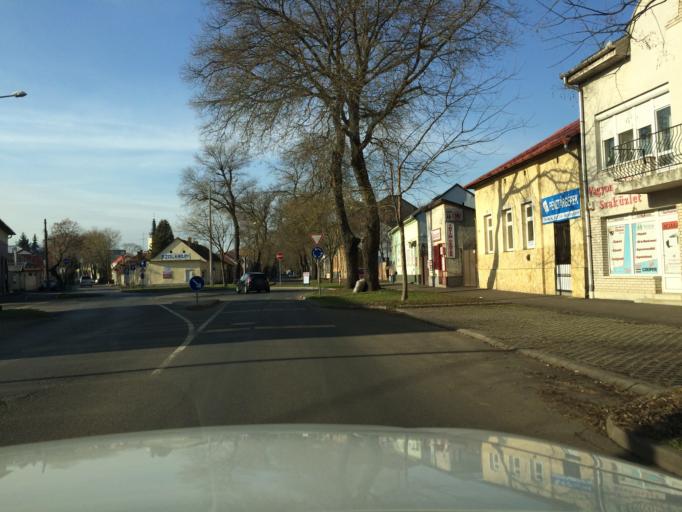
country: HU
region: Szabolcs-Szatmar-Bereg
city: Nyiregyhaza
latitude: 47.9516
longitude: 21.7249
